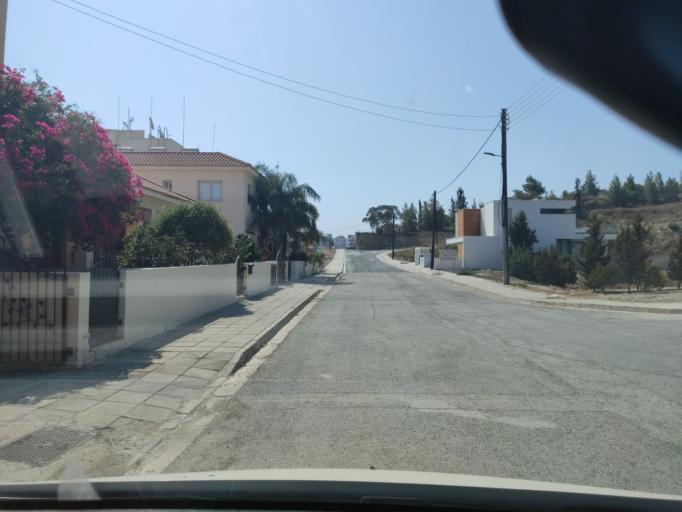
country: CY
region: Lefkosia
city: Geri
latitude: 35.1151
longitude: 33.4187
